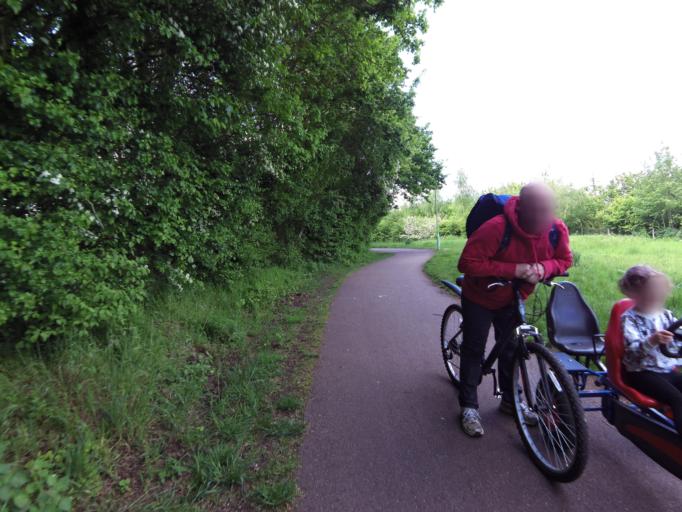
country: GB
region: England
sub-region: Suffolk
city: Great Barton
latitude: 52.2464
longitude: 0.7514
